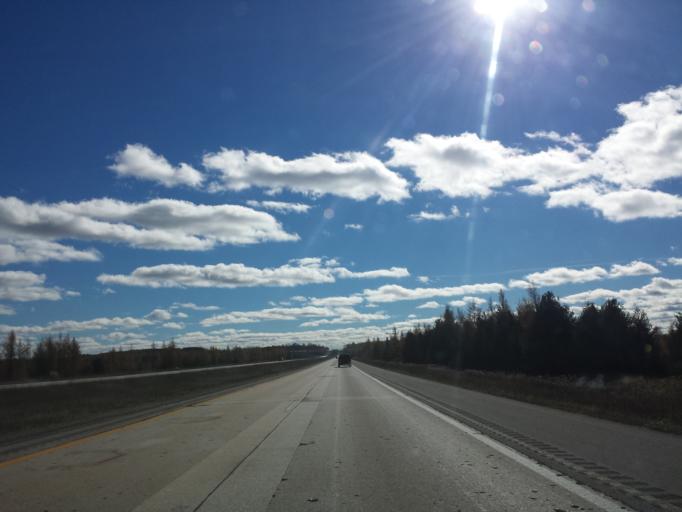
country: US
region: Michigan
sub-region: Cheboygan County
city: Cheboygan
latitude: 45.6501
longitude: -84.6351
